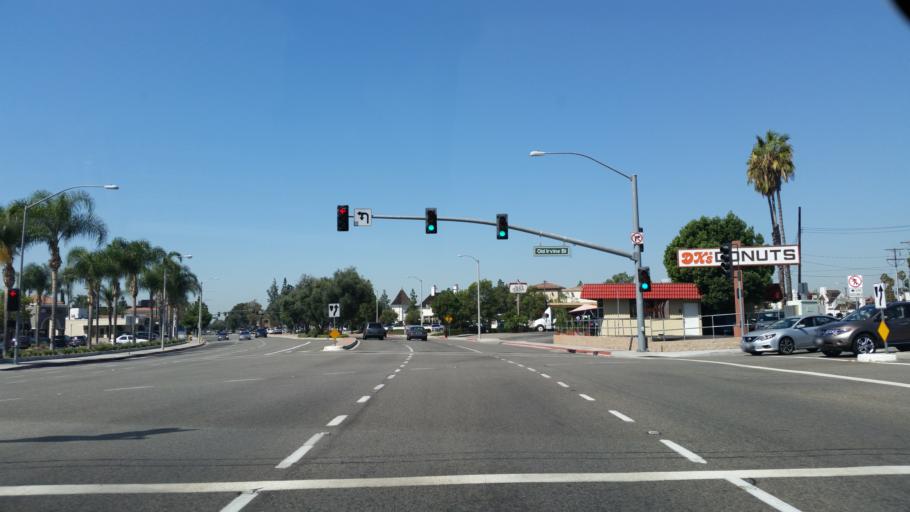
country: US
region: California
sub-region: Orange County
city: Tustin
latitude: 33.7482
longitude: -117.8095
